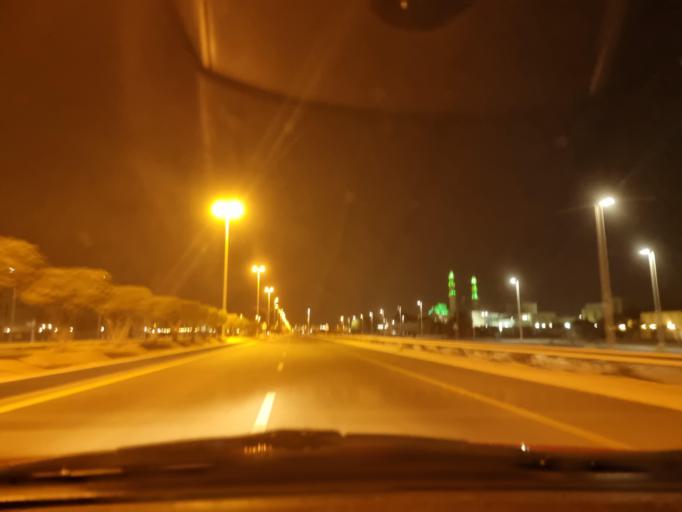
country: AE
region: Abu Dhabi
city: Abu Dhabi
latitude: 24.3721
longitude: 54.7008
